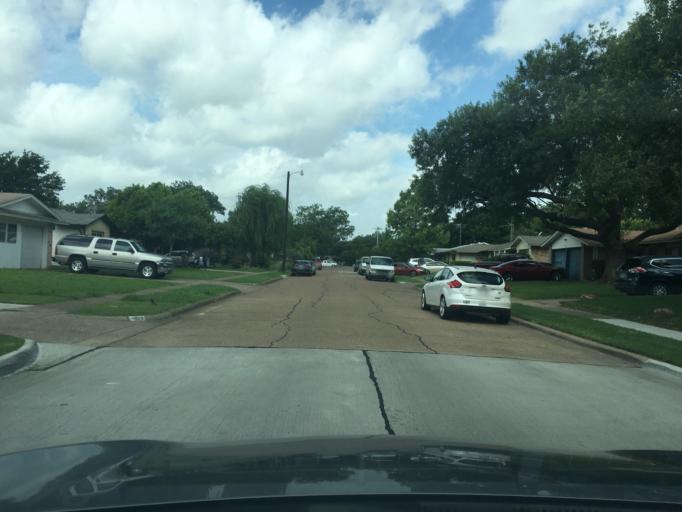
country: US
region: Texas
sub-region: Dallas County
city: Richardson
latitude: 32.9211
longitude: -96.6986
